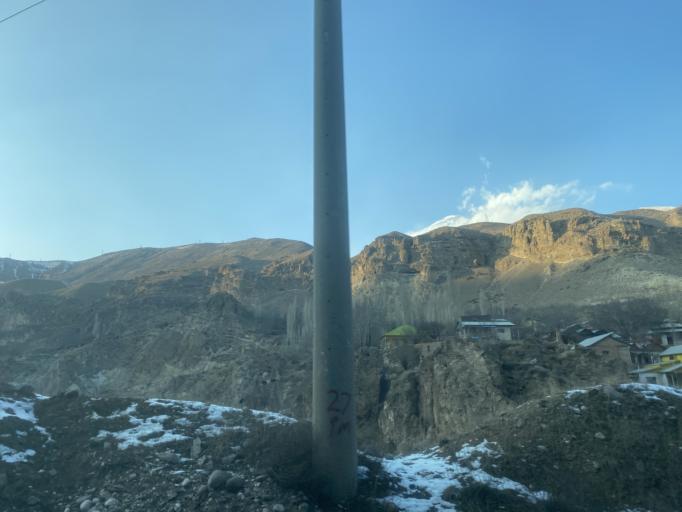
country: IR
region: Tehran
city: Damavand
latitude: 35.8675
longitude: 52.1531
